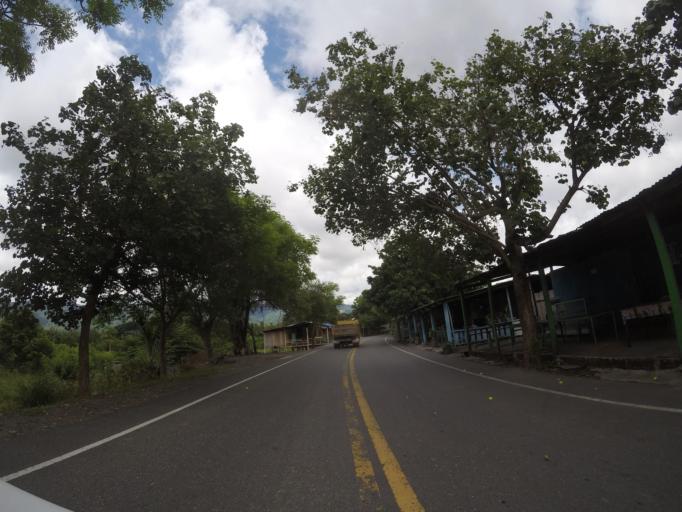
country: TL
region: Liquica
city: Maubara
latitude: -8.7395
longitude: 125.1342
